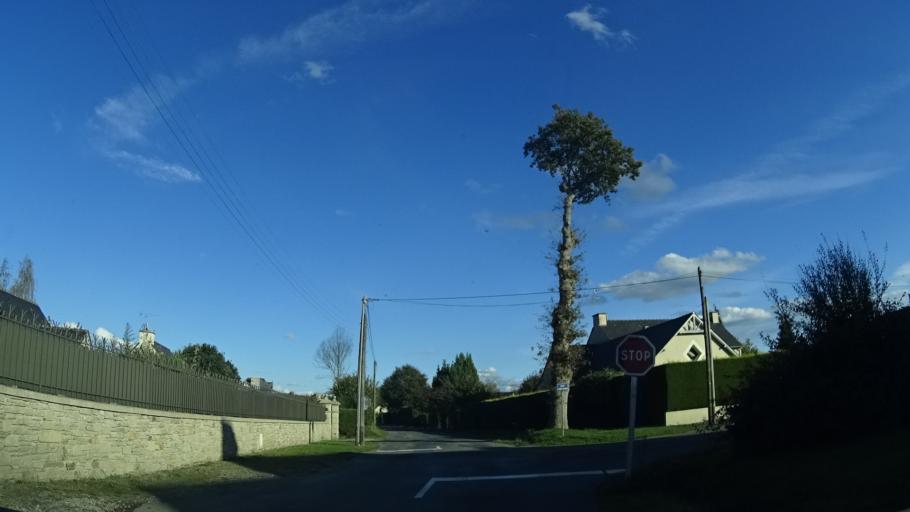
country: FR
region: Brittany
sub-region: Departement d'Ille-et-Vilaine
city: Le Minihic-sur-Rance
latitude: 48.5833
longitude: -2.0112
